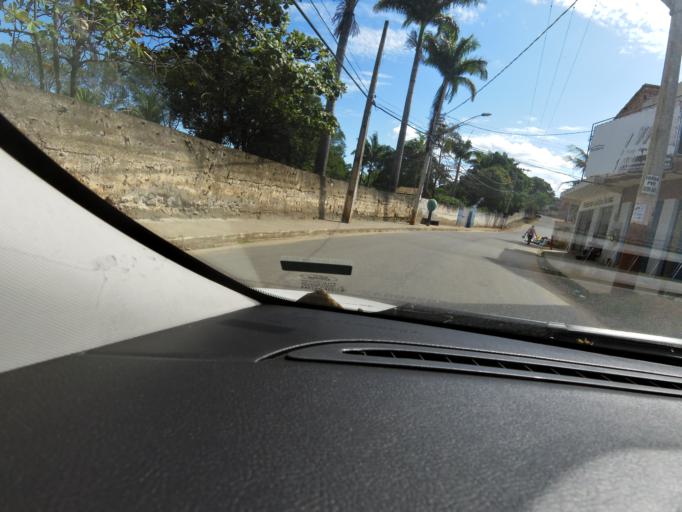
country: BR
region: Espirito Santo
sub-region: Guarapari
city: Guarapari
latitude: -20.6615
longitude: -40.5162
